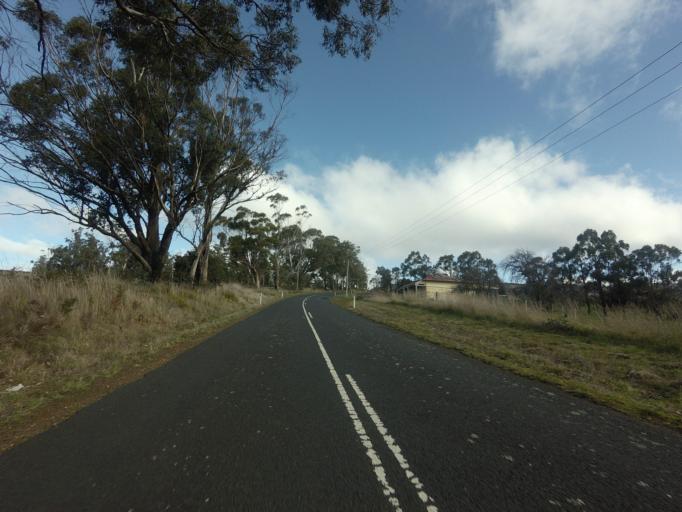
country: AU
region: Tasmania
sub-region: Derwent Valley
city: New Norfolk
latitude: -42.5688
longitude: 146.7009
